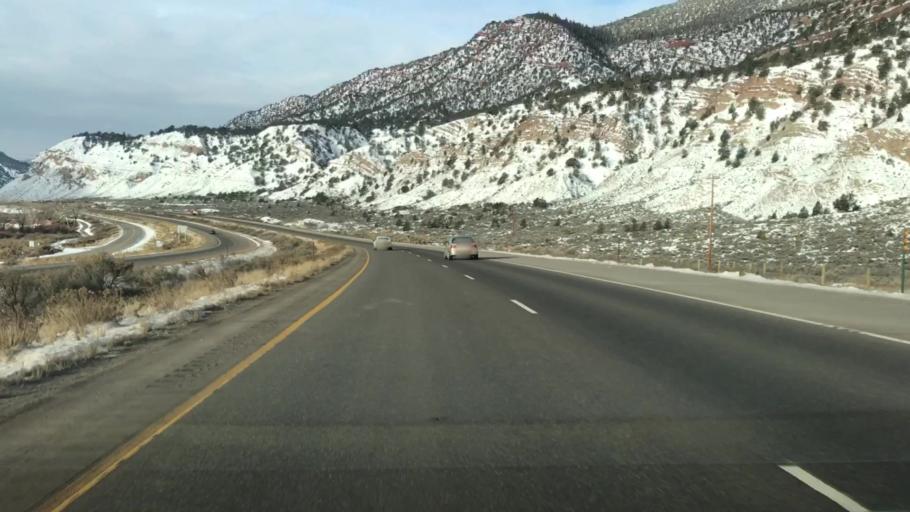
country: US
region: Colorado
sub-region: Eagle County
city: Gypsum
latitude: 39.6564
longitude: -106.9733
